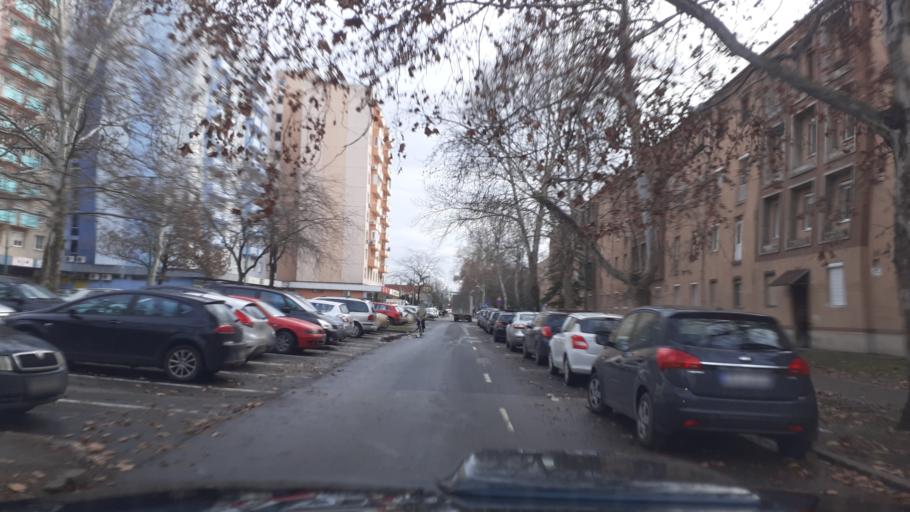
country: HU
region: Fejer
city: dunaujvaros
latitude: 46.9642
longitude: 18.9326
